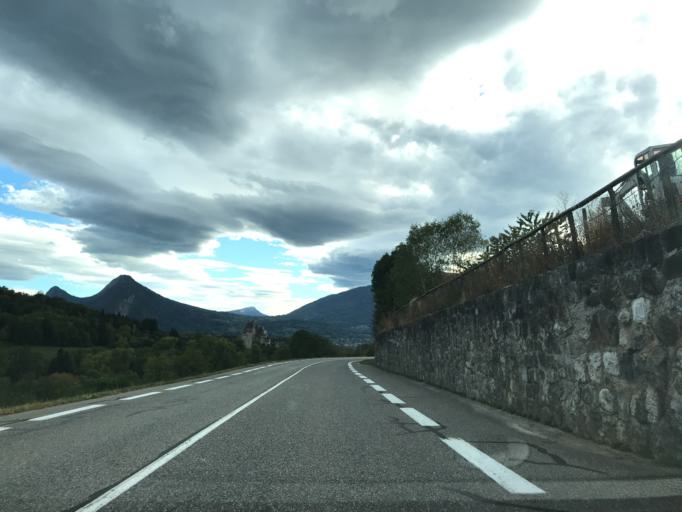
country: FR
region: Rhone-Alpes
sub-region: Departement de la Haute-Savoie
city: Menthon-Saint-Bernard
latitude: 45.8699
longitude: 6.2079
